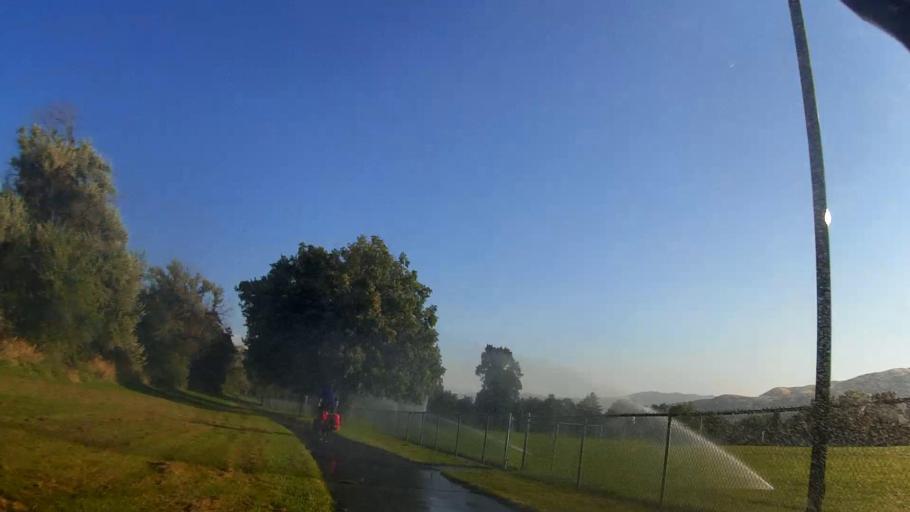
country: US
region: Utah
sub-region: Salt Lake County
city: Salt Lake City
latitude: 40.7846
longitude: -111.9360
